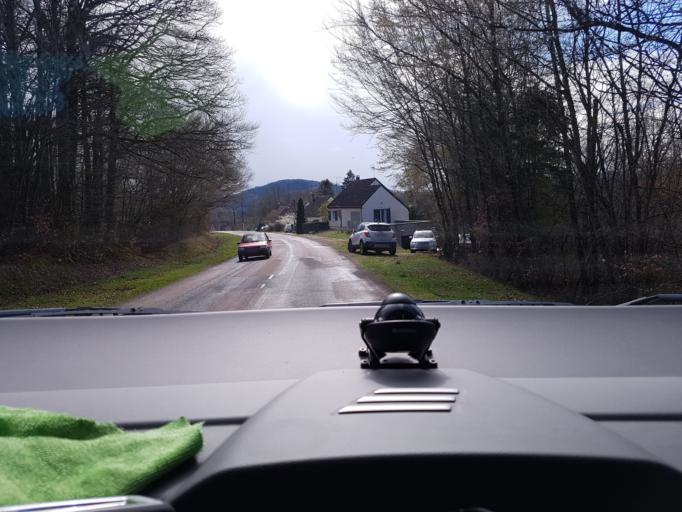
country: FR
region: Bourgogne
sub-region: Departement de la Cote-d'Or
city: Saulieu
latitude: 47.3133
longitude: 4.0343
